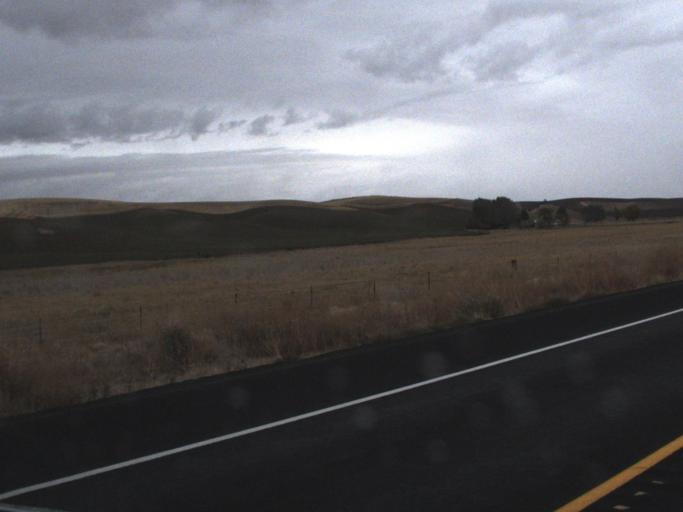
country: US
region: Washington
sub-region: Whitman County
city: Colfax
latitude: 46.8109
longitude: -117.6356
